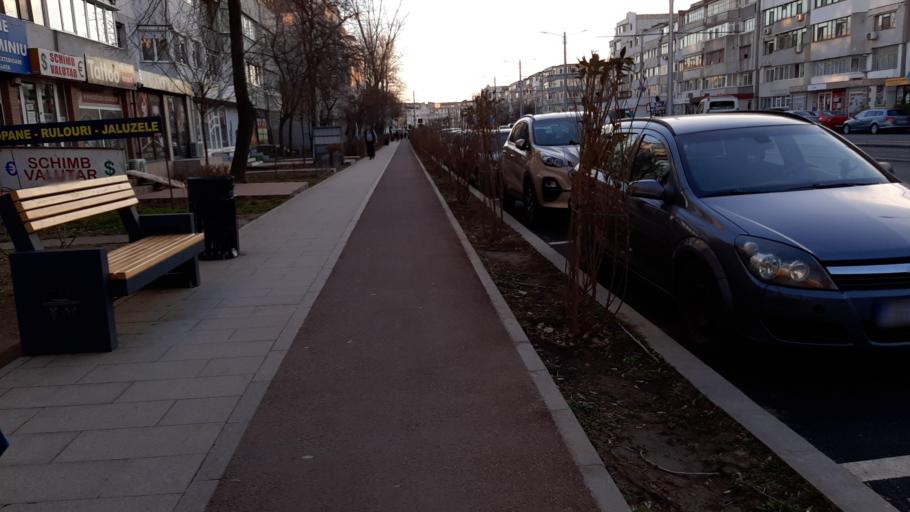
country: RO
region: Galati
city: Galati
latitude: 45.4436
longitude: 28.0226
